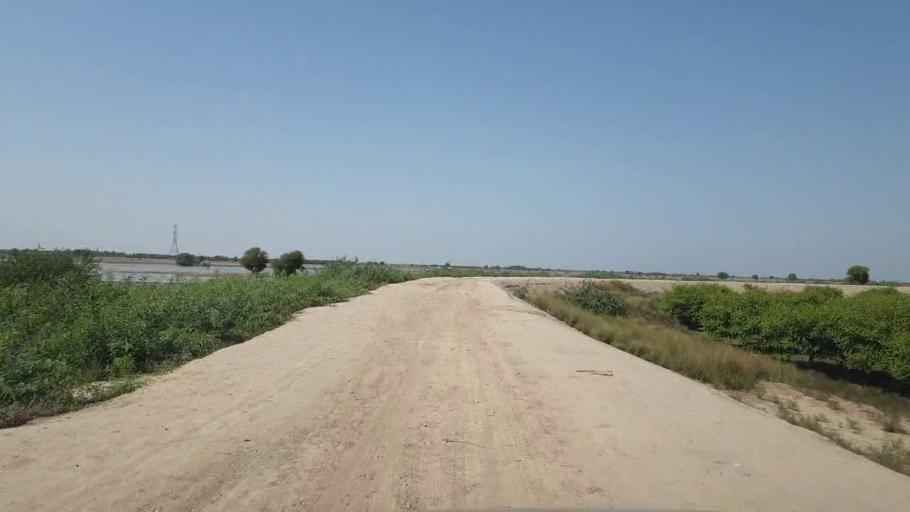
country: PK
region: Sindh
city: Matiari
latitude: 25.6367
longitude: 68.4866
